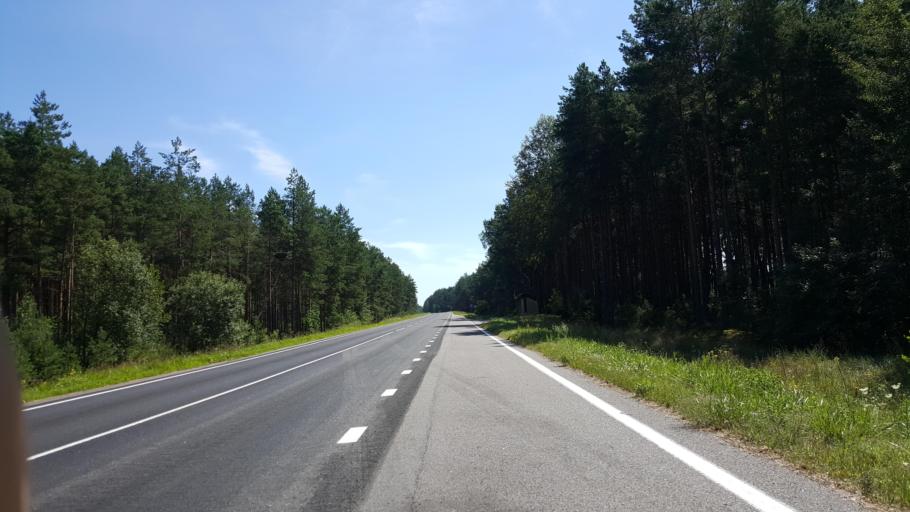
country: BY
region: Brest
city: Zhabinka
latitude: 52.3984
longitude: 24.0201
